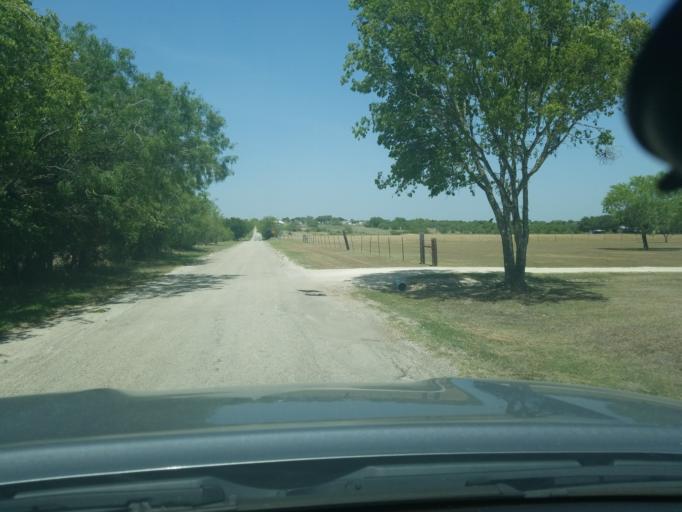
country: US
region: Texas
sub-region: Guadalupe County
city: Marion
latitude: 29.5741
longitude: -98.1831
